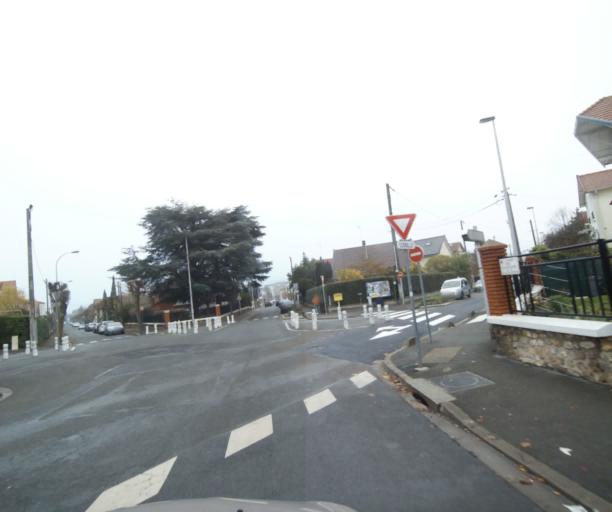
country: FR
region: Ile-de-France
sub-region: Departement de Seine-Saint-Denis
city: Gagny
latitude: 48.8780
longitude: 2.5249
